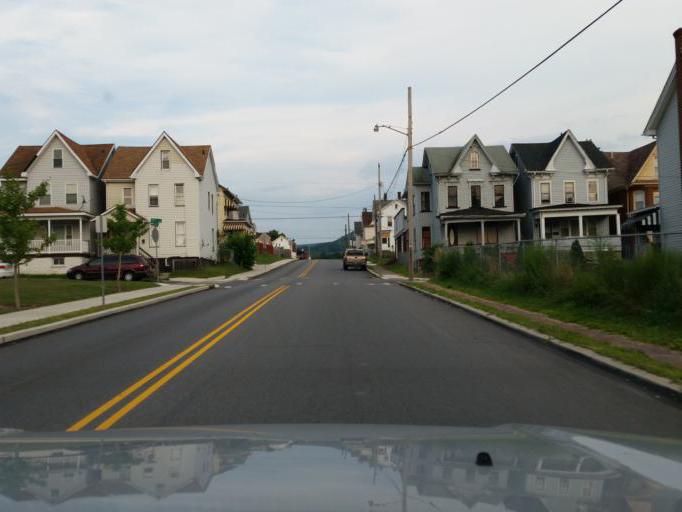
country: US
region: Pennsylvania
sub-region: Blair County
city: Altoona
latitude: 40.5235
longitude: -78.3855
